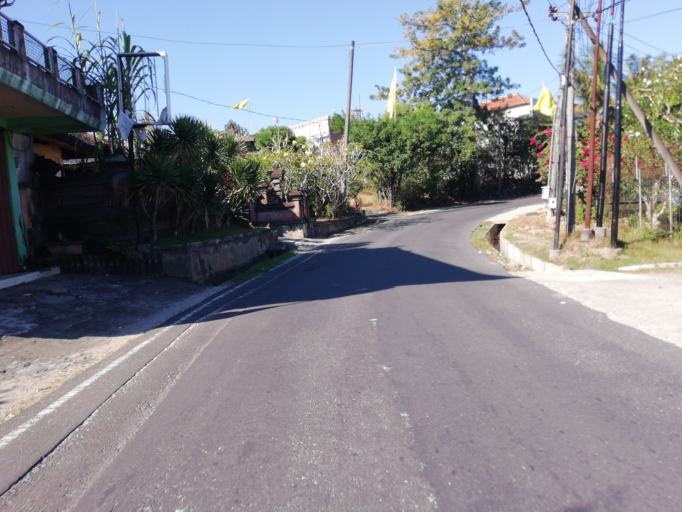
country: ID
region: Bali
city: Jimbaran
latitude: -8.8265
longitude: 115.1687
